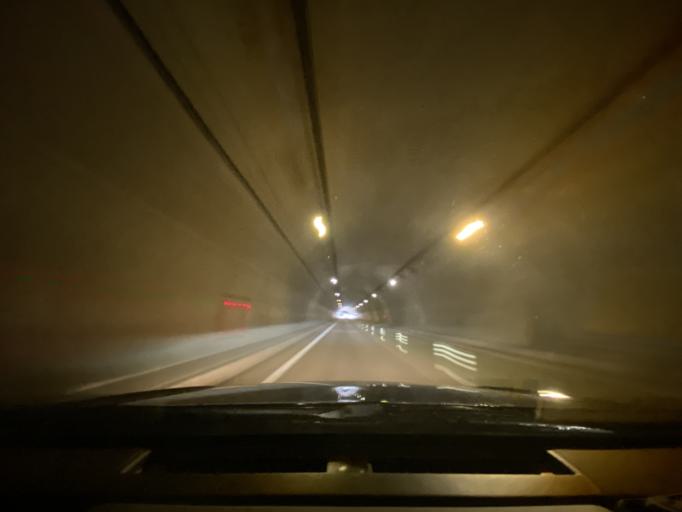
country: JP
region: Hokkaido
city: Kitami
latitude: 43.7765
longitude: 143.8883
